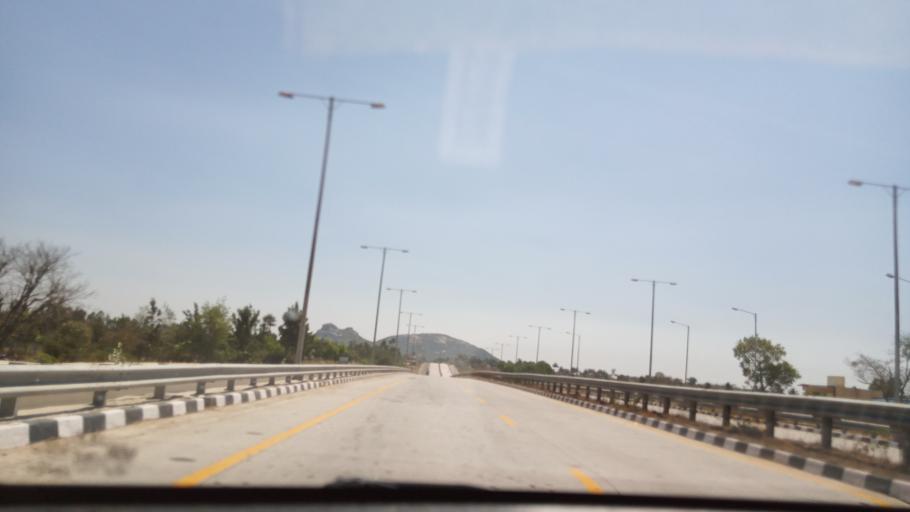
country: IN
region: Andhra Pradesh
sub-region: Chittoor
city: Palmaner
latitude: 13.1843
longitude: 78.6107
